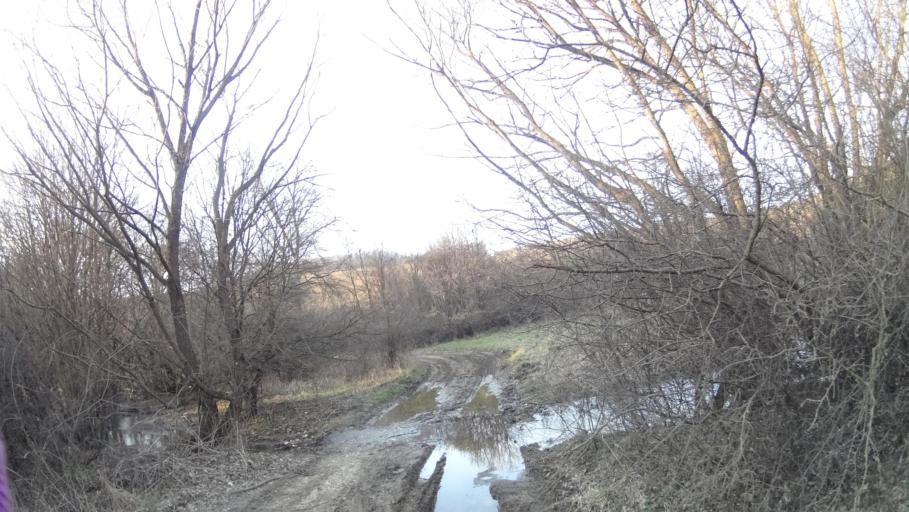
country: HU
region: Pest
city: Kosd
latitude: 47.8469
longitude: 19.1572
